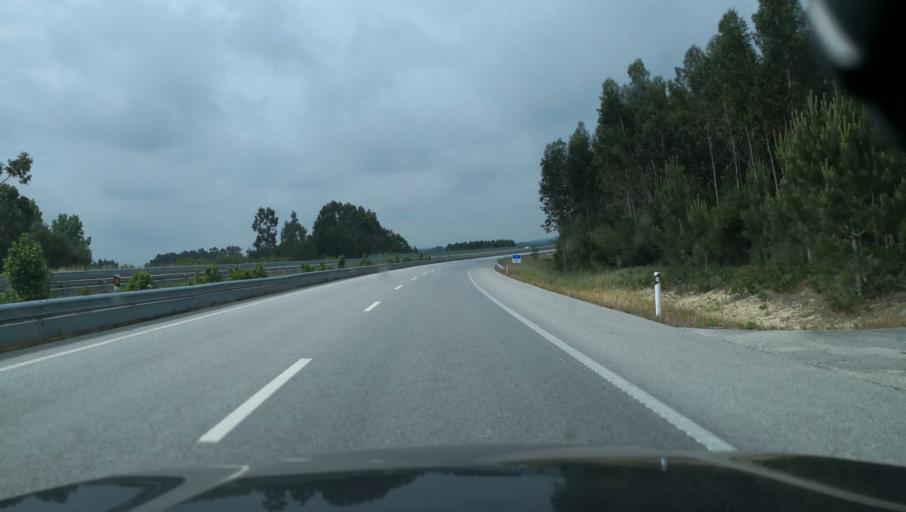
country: PT
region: Coimbra
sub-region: Figueira da Foz
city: Alhadas
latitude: 40.2575
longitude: -8.7624
